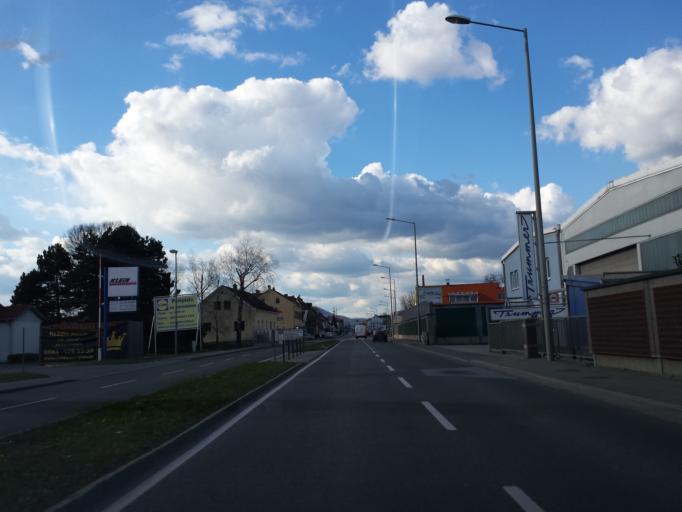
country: AT
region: Styria
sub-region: Politischer Bezirk Graz-Umgebung
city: Feldkirchen bei Graz
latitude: 47.0227
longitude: 15.4368
